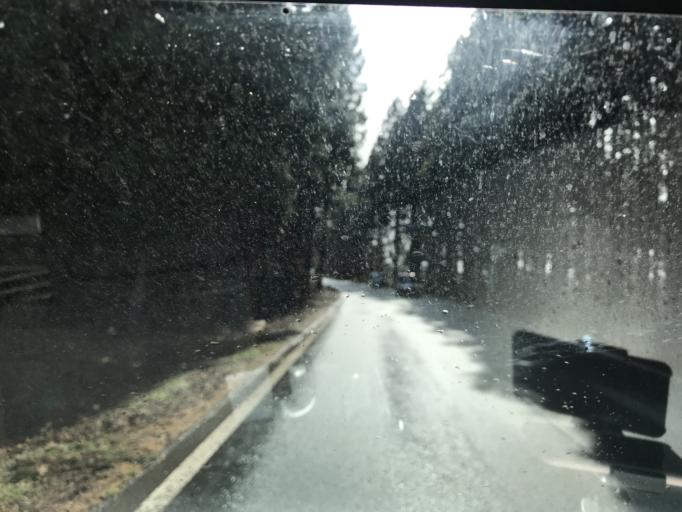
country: JP
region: Iwate
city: Kitakami
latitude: 39.2761
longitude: 141.0507
